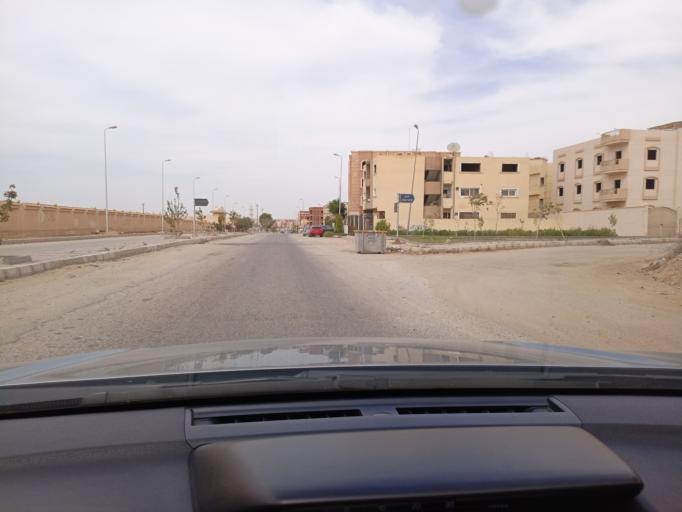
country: EG
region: Muhafazat al Qalyubiyah
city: Al Khankah
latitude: 30.2458
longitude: 31.4947
